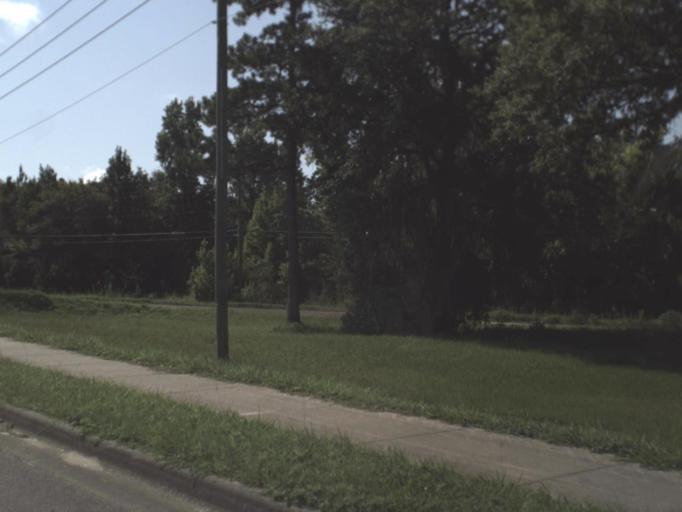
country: US
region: Florida
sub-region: Hernando County
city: South Brooksville
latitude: 28.5386
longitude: -82.3982
